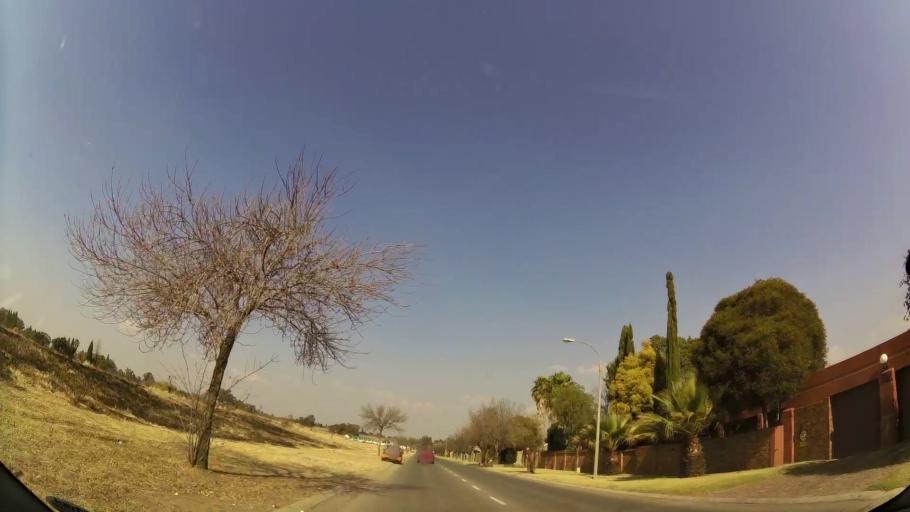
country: ZA
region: Gauteng
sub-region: Ekurhuleni Metropolitan Municipality
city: Benoni
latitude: -26.1435
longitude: 28.2875
